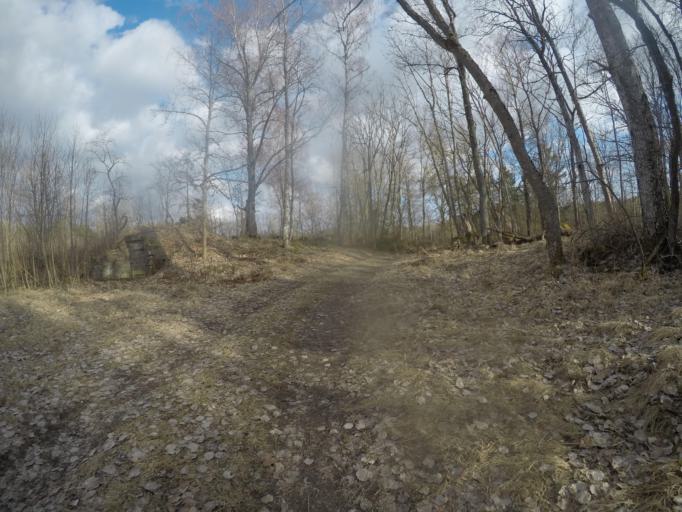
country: SE
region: Soedermanland
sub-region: Eskilstuna Kommun
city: Hallbybrunn
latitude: 59.3855
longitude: 16.3994
